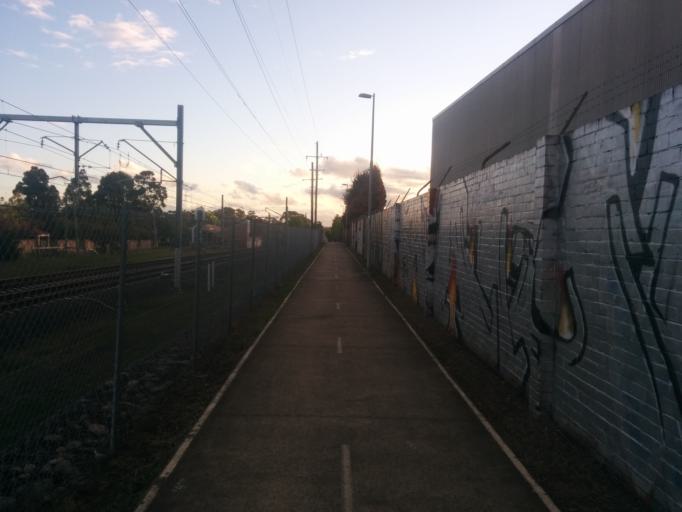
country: AU
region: New South Wales
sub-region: Fairfield
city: Fairfield East
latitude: -33.8665
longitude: 150.9674
